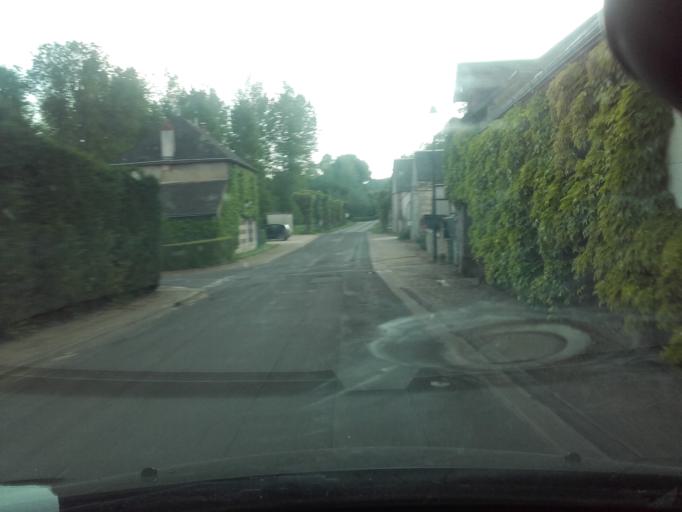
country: FR
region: Centre
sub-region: Departement du Loir-et-Cher
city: Chouzy-sur-Cisse
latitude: 47.5619
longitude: 1.2128
